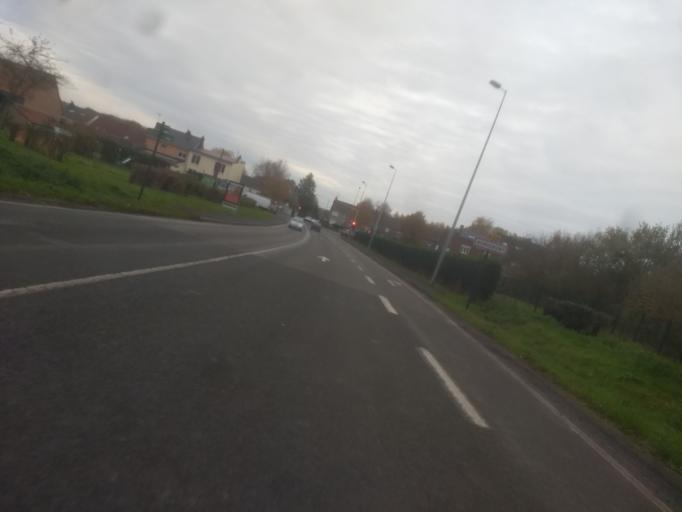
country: FR
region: Nord-Pas-de-Calais
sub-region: Departement du Pas-de-Calais
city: Achicourt
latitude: 50.2676
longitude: 2.7521
